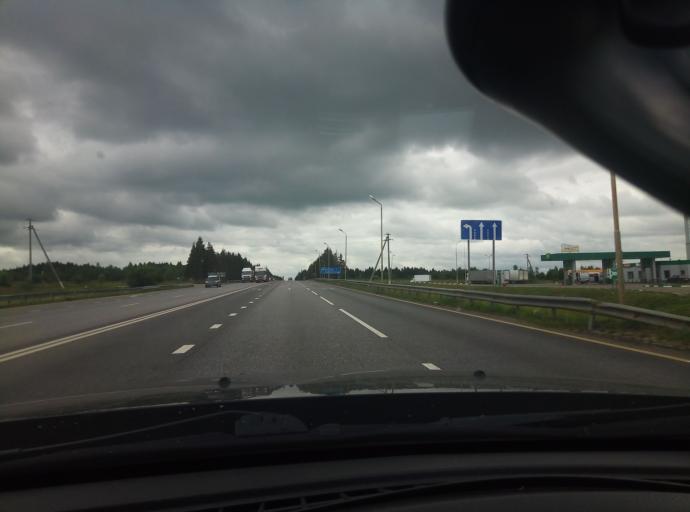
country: RU
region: Kaluga
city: Maloyaroslavets
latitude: 55.0087
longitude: 36.5416
